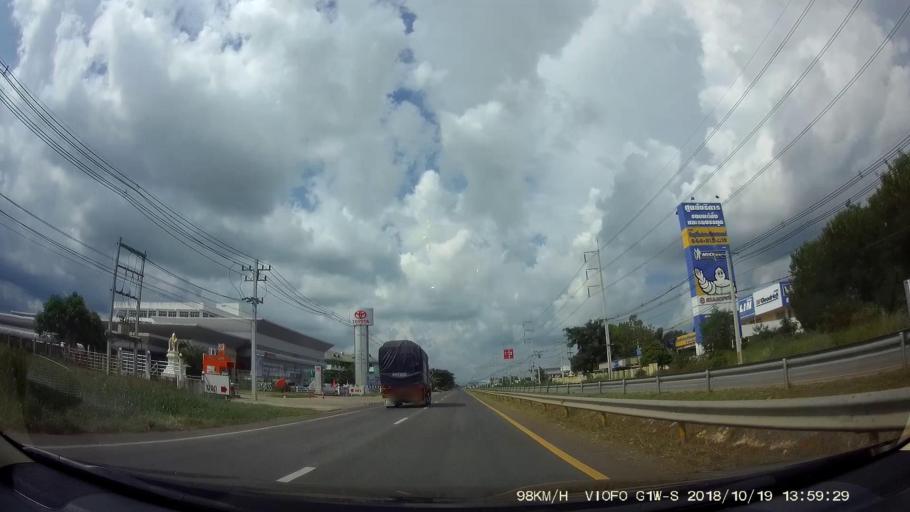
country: TH
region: Chaiyaphum
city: Chaiyaphum
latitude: 15.8102
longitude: 102.0608
